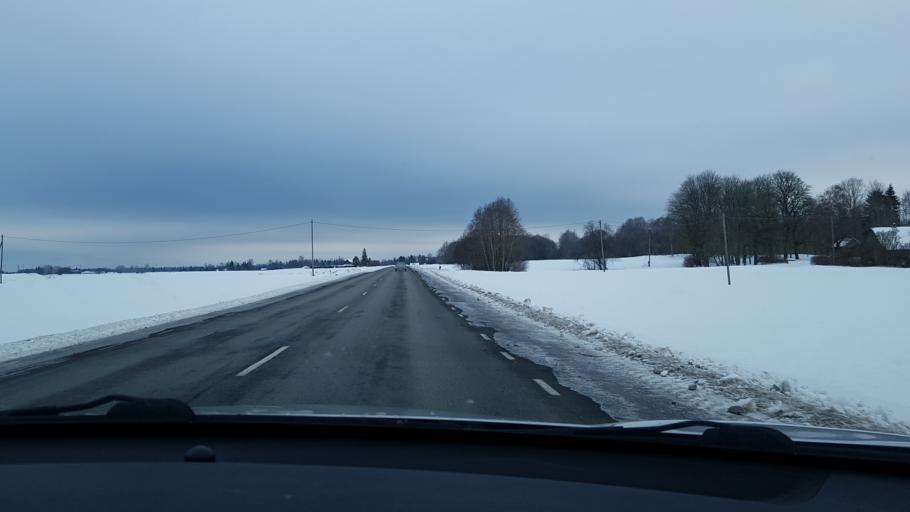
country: EE
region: Jaervamaa
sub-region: Paide linn
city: Paide
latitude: 58.8850
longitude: 25.7085
